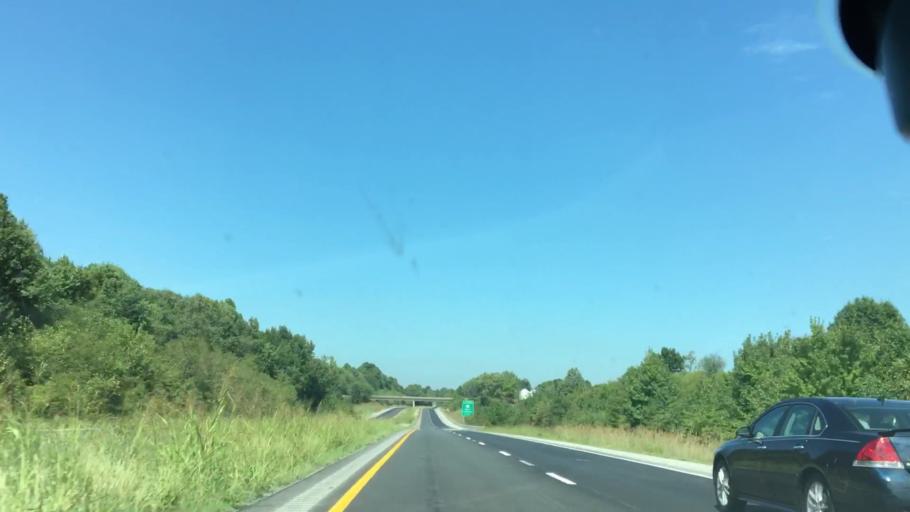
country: US
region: Kentucky
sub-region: Hopkins County
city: Madisonville
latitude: 37.4543
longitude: -87.4785
